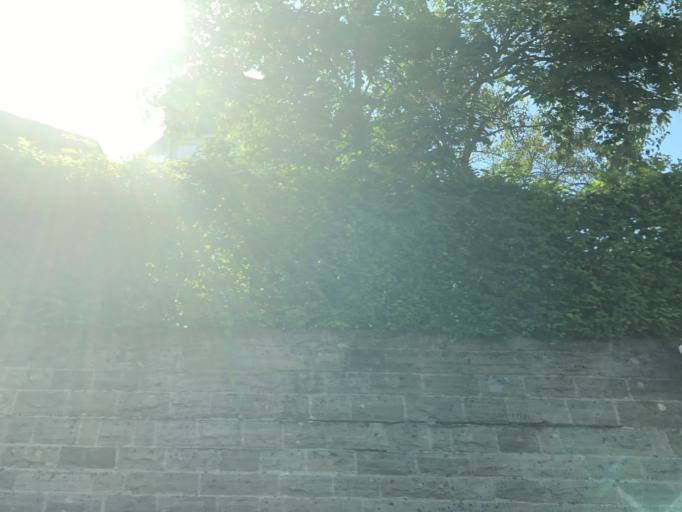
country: DE
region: Baden-Wuerttemberg
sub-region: Tuebingen Region
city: Wangen im Allgau
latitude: 47.6933
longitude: 9.8404
